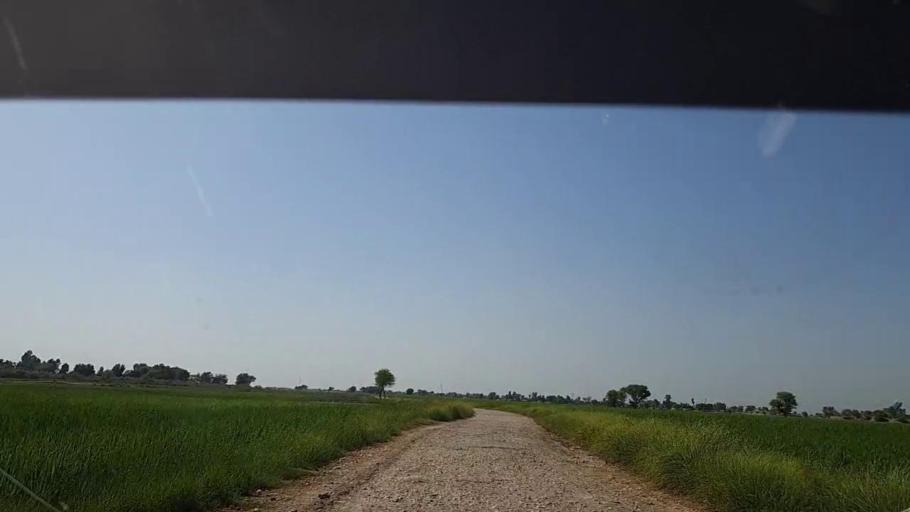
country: PK
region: Sindh
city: Ghauspur
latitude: 28.1801
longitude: 69.0319
